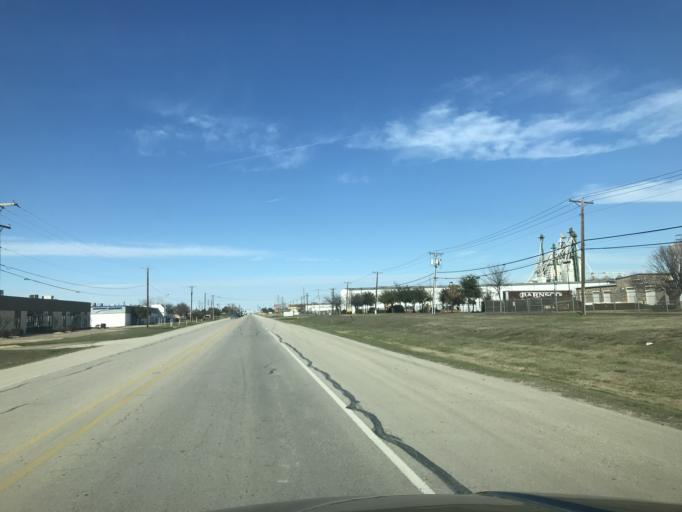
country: US
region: Texas
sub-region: Tarrant County
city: Blue Mound
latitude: 32.8293
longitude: -97.3429
